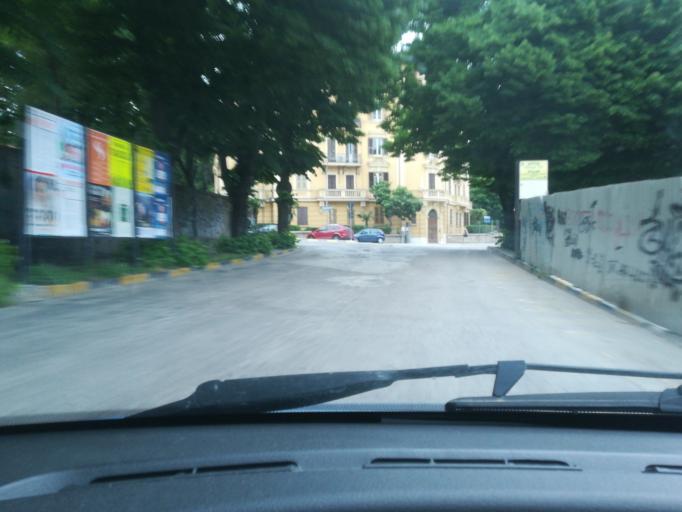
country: IT
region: The Marches
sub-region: Provincia di Macerata
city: Macerata
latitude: 43.2999
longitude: 13.4445
